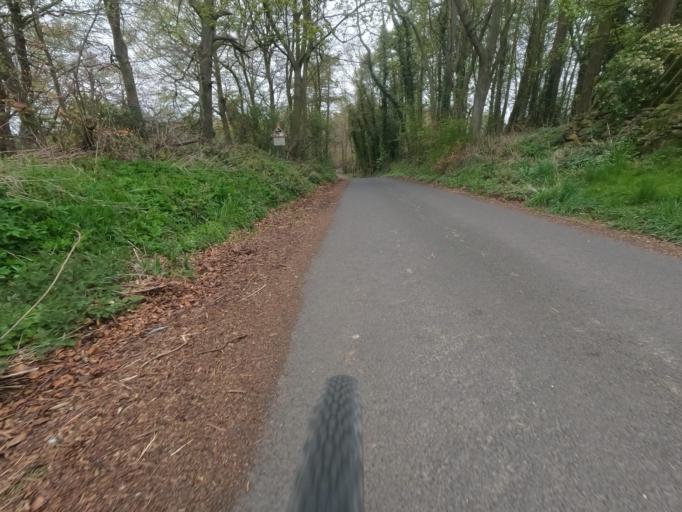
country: GB
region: England
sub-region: Northumberland
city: Meldon
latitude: 55.0719
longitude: -1.8173
